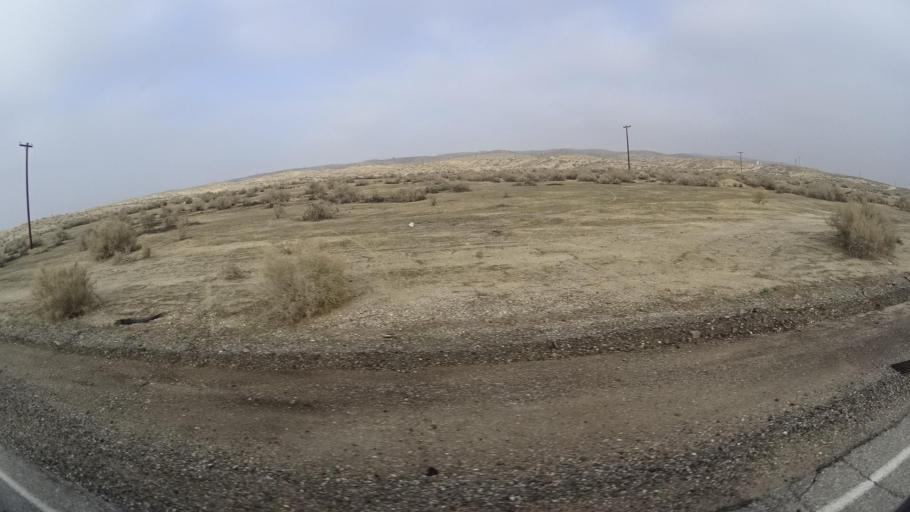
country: US
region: California
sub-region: Kern County
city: South Taft
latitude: 35.1353
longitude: -119.4074
